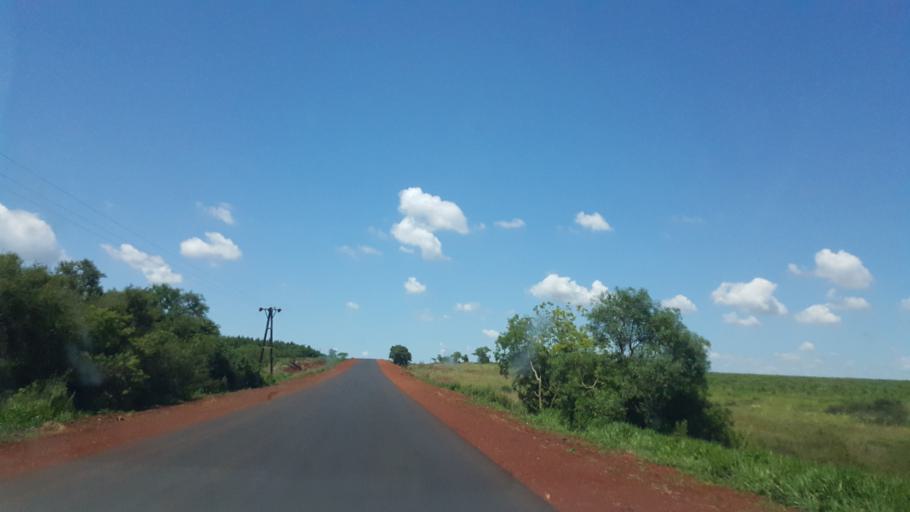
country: AR
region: Corrientes
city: Santo Tome
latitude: -28.4715
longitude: -56.0288
